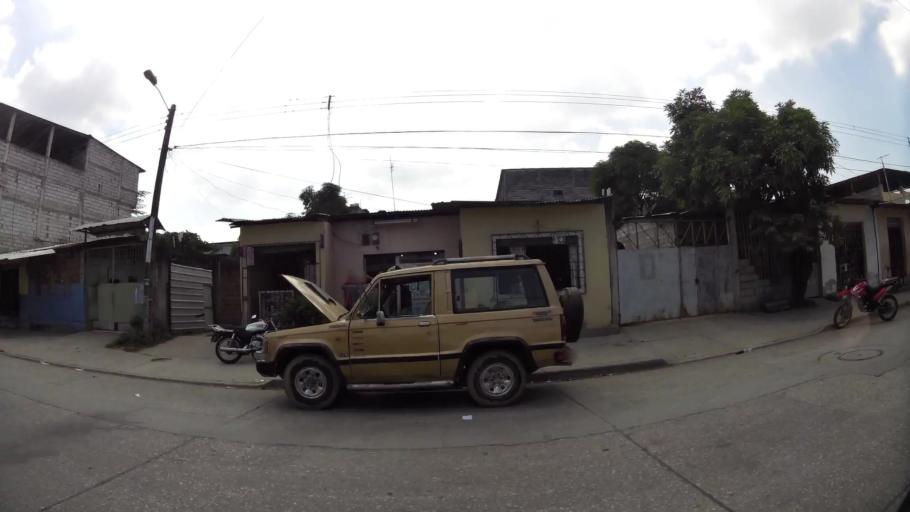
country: EC
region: Guayas
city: Santa Lucia
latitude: -2.1326
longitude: -79.9425
